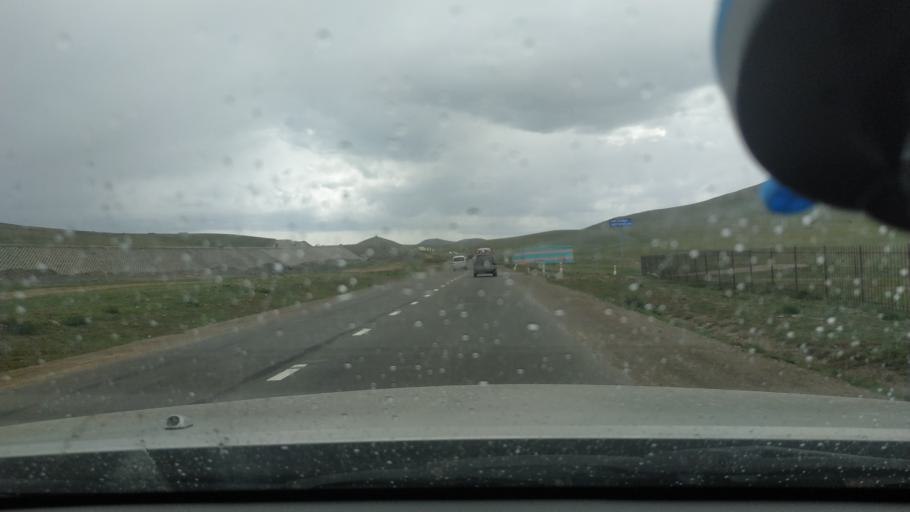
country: MN
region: Ulaanbaatar
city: Ulaanbaatar
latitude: 47.7984
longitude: 106.7459
